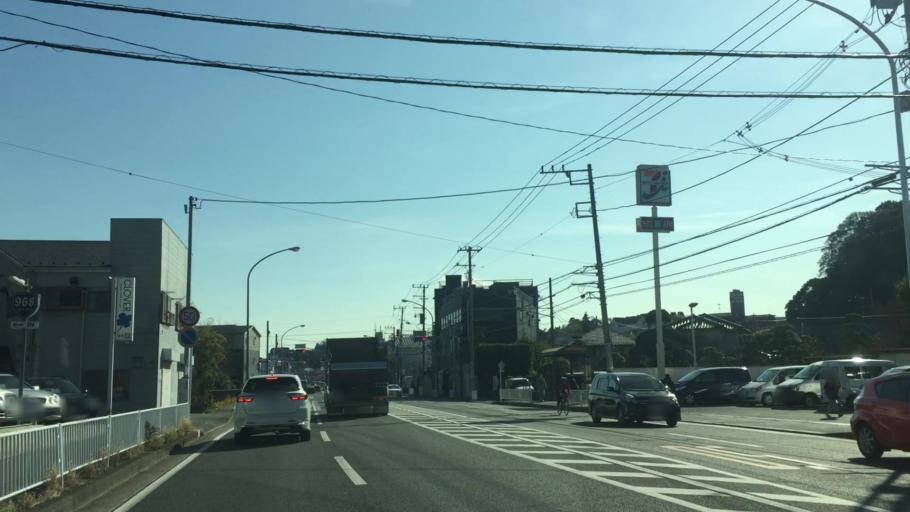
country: JP
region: Kanagawa
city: Yokohama
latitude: 35.3740
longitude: 139.6109
